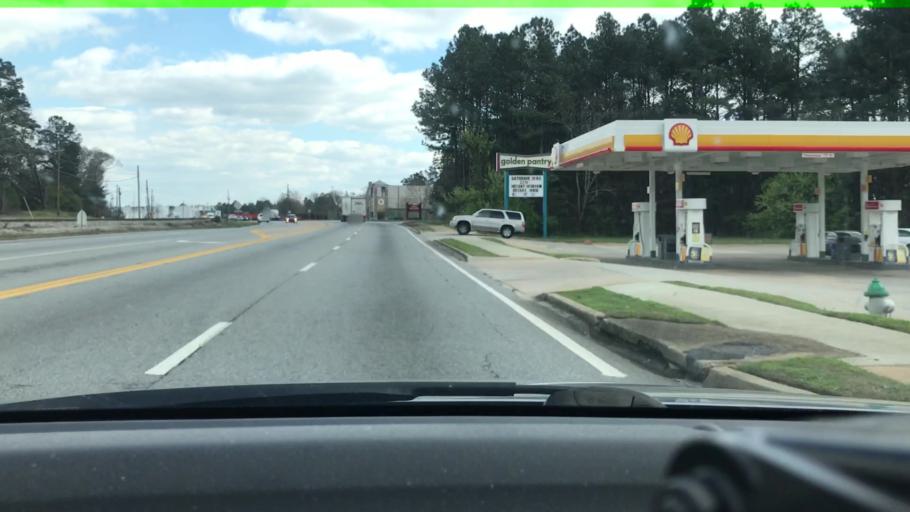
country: US
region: Georgia
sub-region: Clarke County
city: Country Club Estates
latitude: 33.9900
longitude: -83.4298
